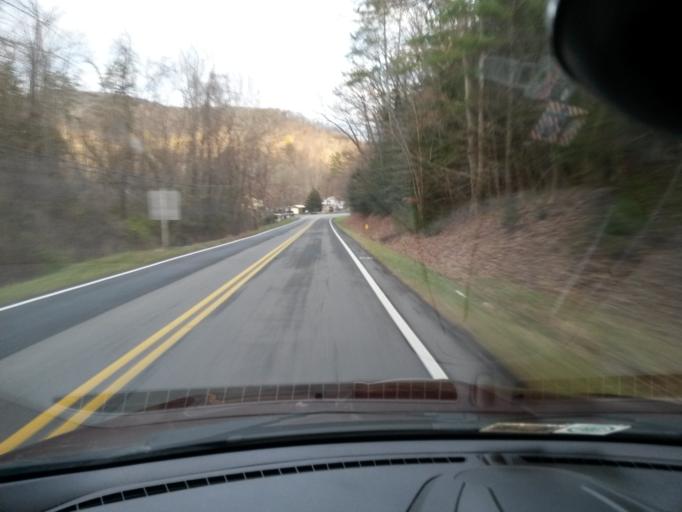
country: US
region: Virginia
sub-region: City of Covington
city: Covington
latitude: 37.8063
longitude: -80.0688
